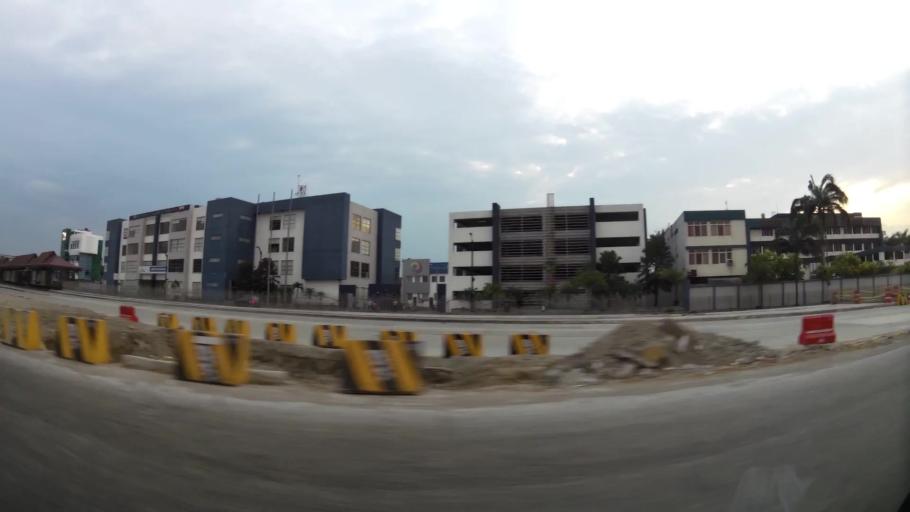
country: EC
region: Guayas
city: Guayaquil
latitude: -2.1759
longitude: -79.8916
